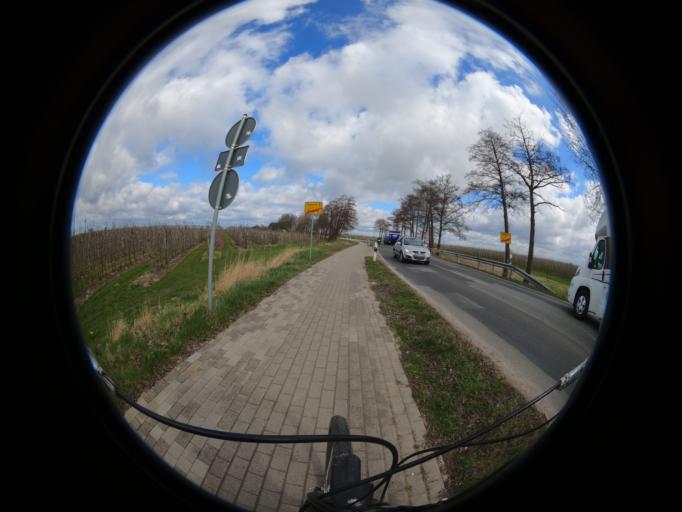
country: DE
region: Lower Saxony
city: Neu Wulmstorf
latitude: 53.4999
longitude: 9.7818
